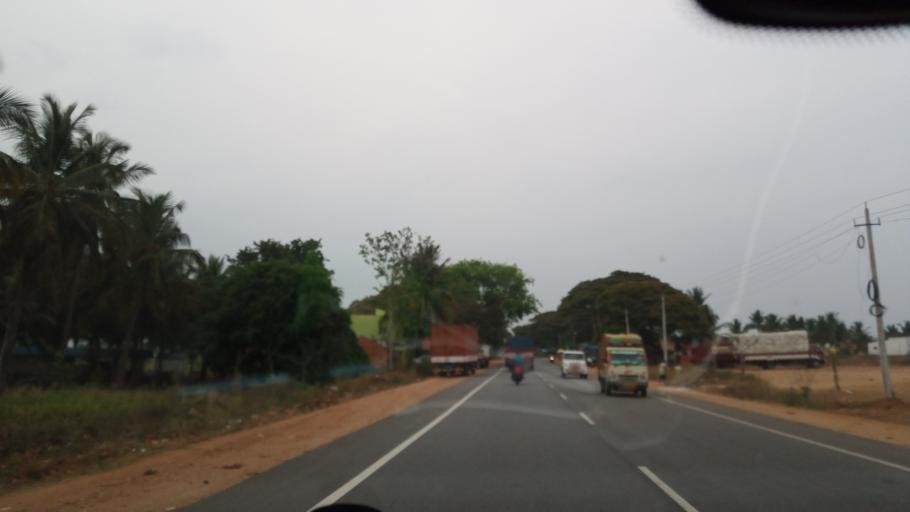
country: IN
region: Karnataka
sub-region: Mandya
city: Nagamangala
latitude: 12.7882
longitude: 76.7495
